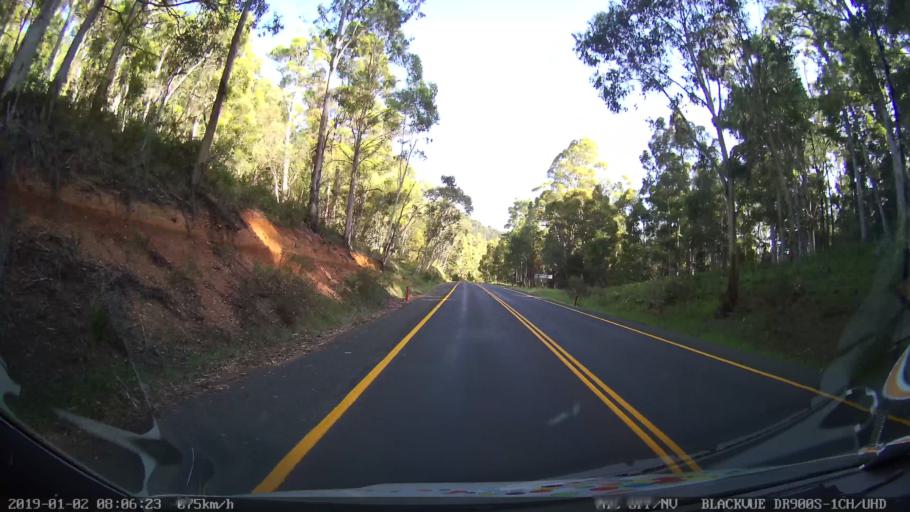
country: AU
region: New South Wales
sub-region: Tumut Shire
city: Tumut
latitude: -35.6406
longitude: 148.3871
